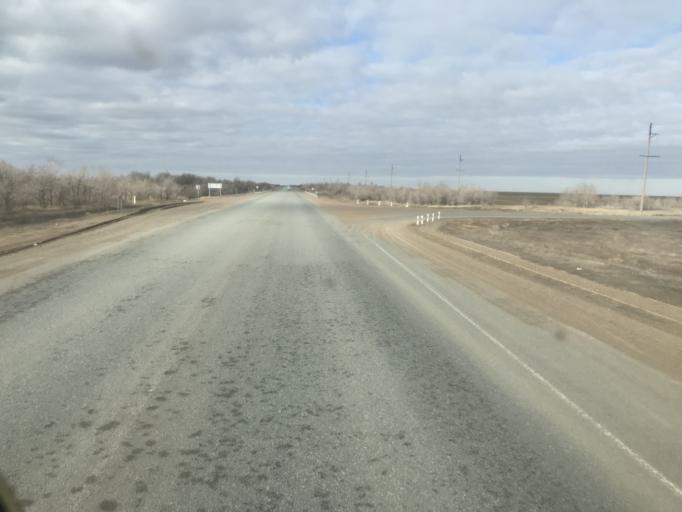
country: KZ
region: Batys Qazaqstan
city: Krugloozernoe
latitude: 51.1931
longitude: 51.0924
